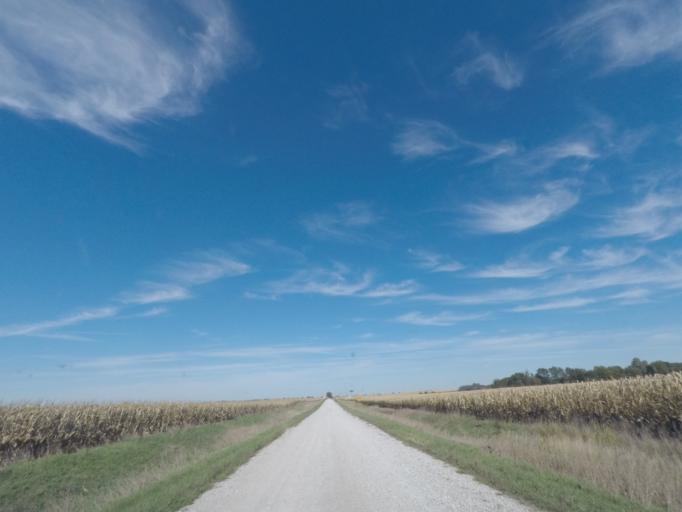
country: US
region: Iowa
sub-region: Story County
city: Nevada
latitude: 42.0163
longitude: -93.3573
